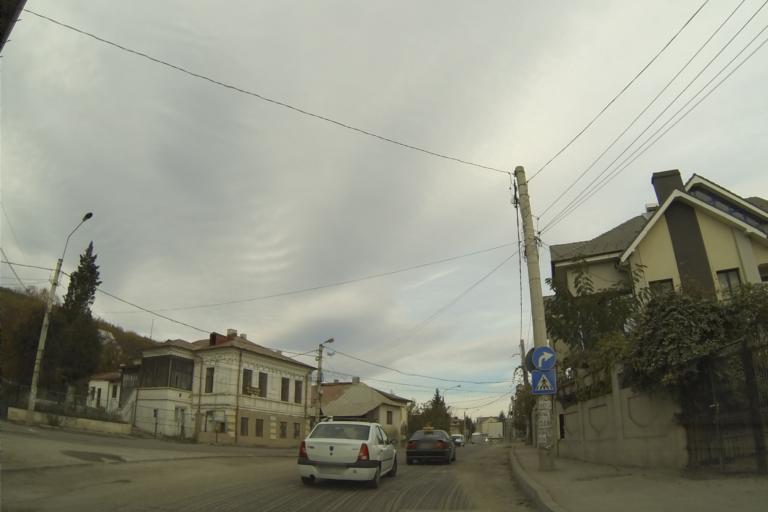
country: RO
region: Olt
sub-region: Municipiul Slatina
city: Slatina
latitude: 44.4259
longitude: 24.3528
